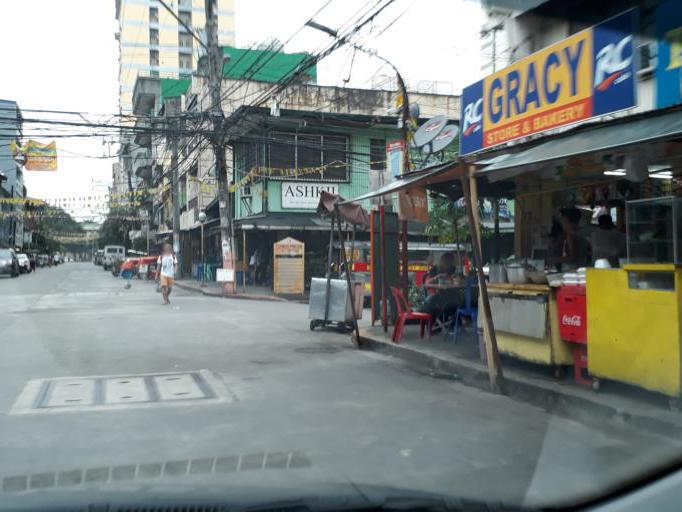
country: PH
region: Metro Manila
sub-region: City of Manila
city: Manila
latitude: 14.6067
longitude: 120.9876
